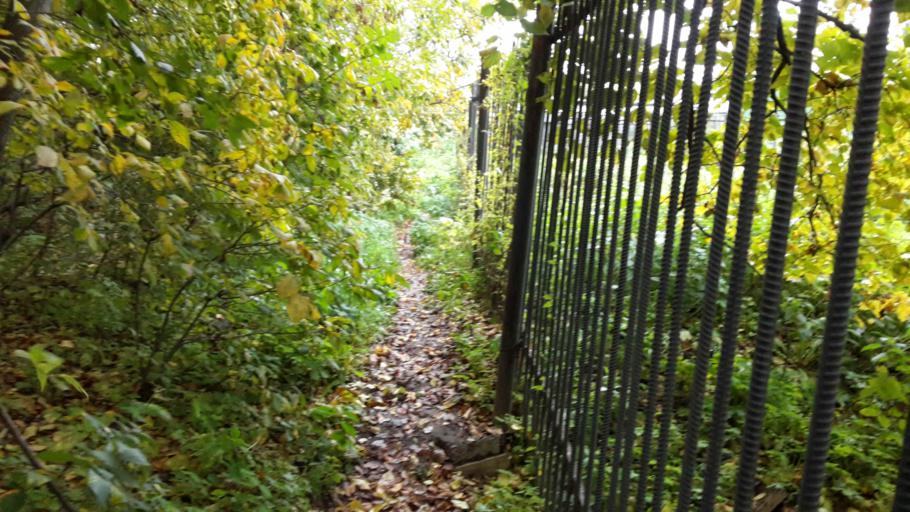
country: RU
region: Moskovskaya
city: Kur'yanovo
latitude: 55.6397
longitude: 37.7015
